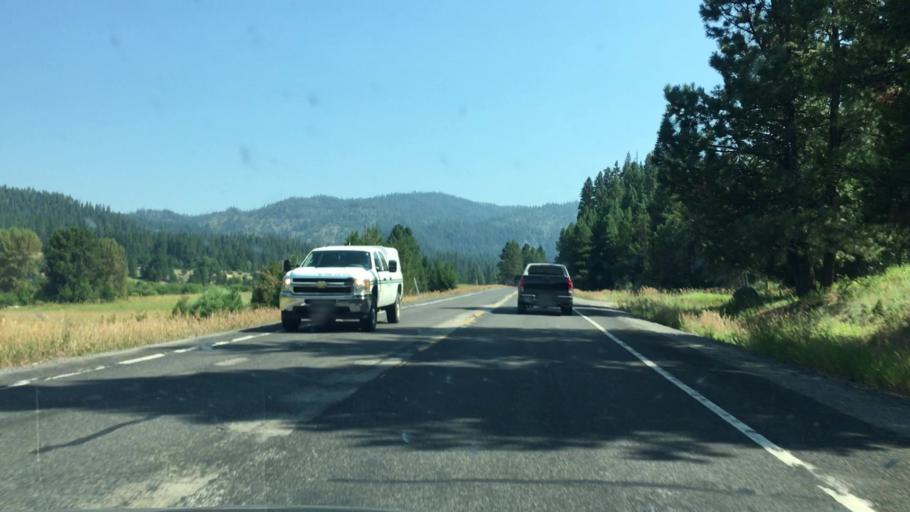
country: US
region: Idaho
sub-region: Valley County
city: Cascade
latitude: 44.2924
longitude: -116.0825
